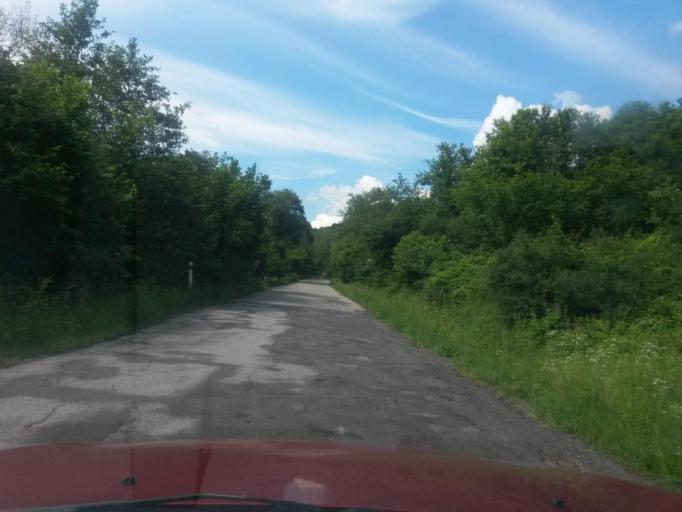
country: UA
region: Zakarpattia
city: Velykyi Bereznyi
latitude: 48.9151
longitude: 22.3720
